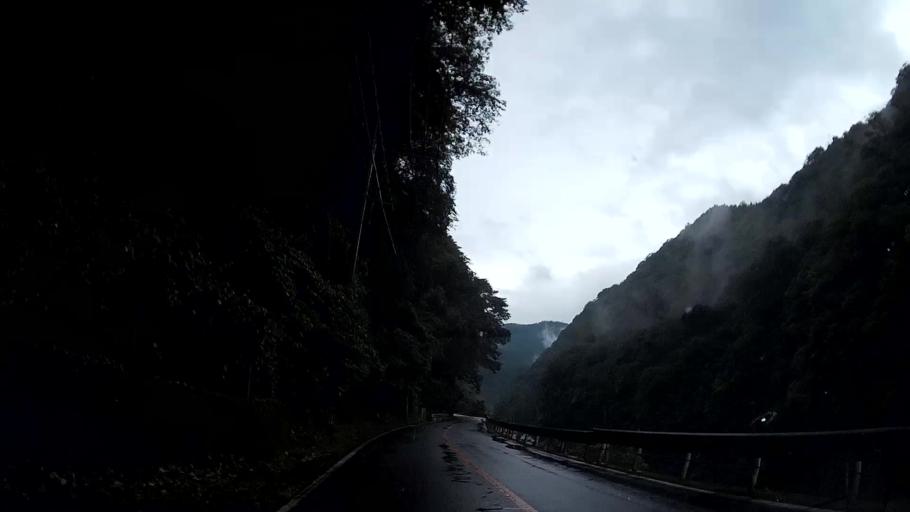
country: JP
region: Oita
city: Hita
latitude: 33.1803
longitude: 131.0186
